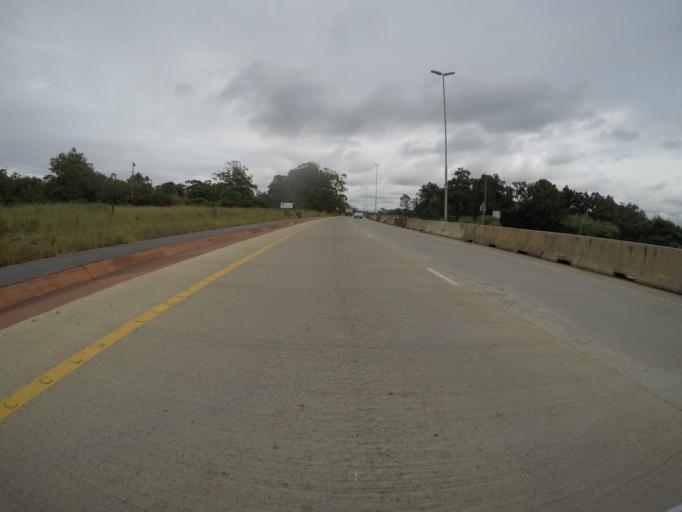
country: ZA
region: Eastern Cape
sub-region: Buffalo City Metropolitan Municipality
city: East London
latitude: -32.9422
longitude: 27.9637
